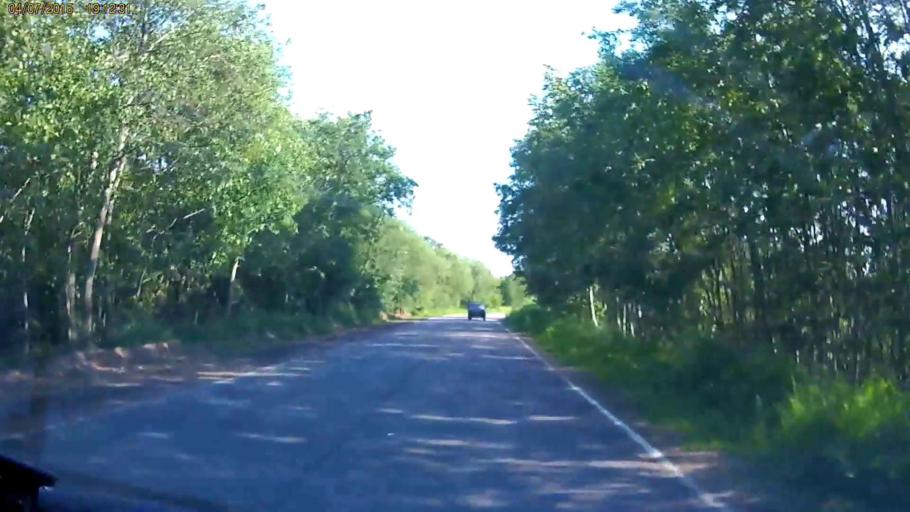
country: RU
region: Leningrad
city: Garbolovo
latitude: 60.3161
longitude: 30.4930
